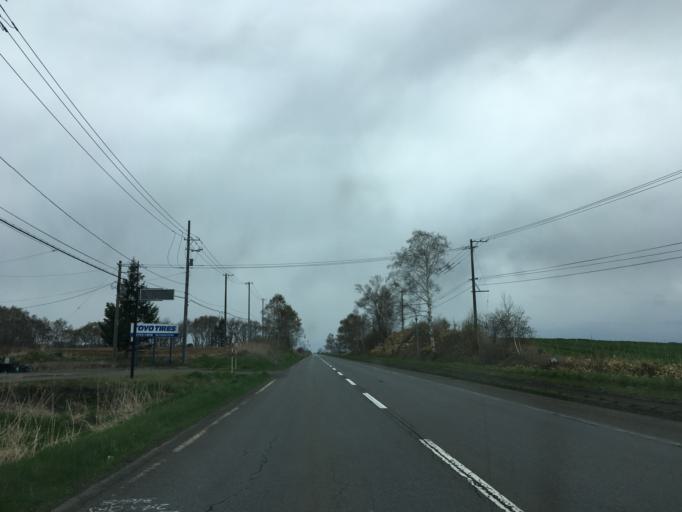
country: JP
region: Hokkaido
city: Chitose
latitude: 42.9175
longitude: 141.8098
